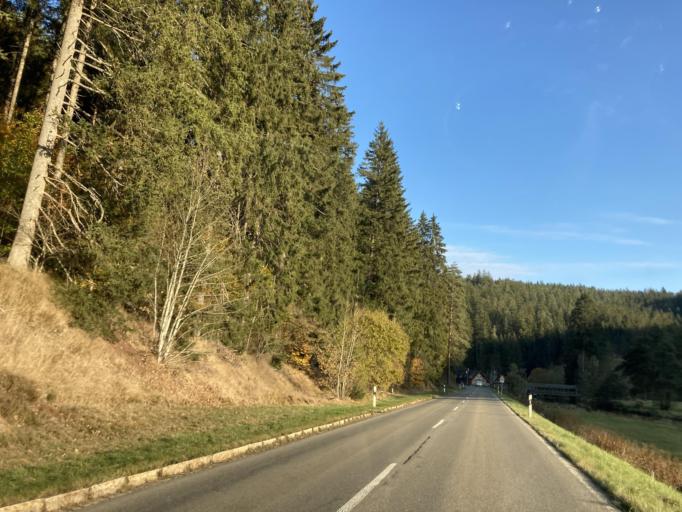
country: DE
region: Baden-Wuerttemberg
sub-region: Freiburg Region
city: Vohrenbach
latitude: 47.9899
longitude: 8.3549
